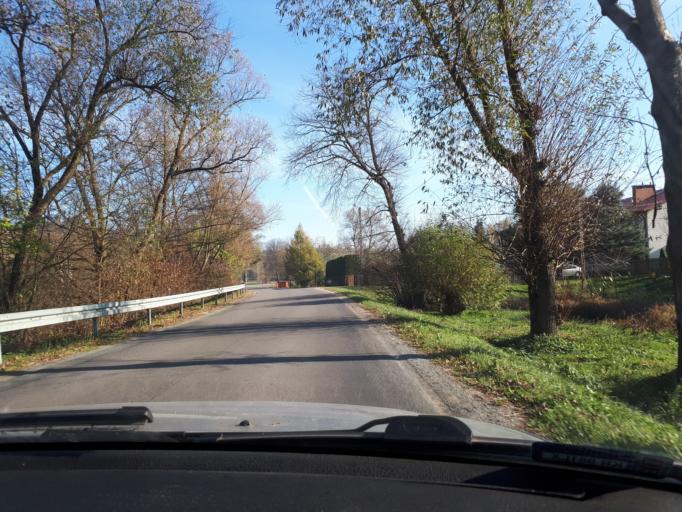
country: PL
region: Subcarpathian Voivodeship
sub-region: Powiat debicki
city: Debica
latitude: 50.0049
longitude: 21.3966
